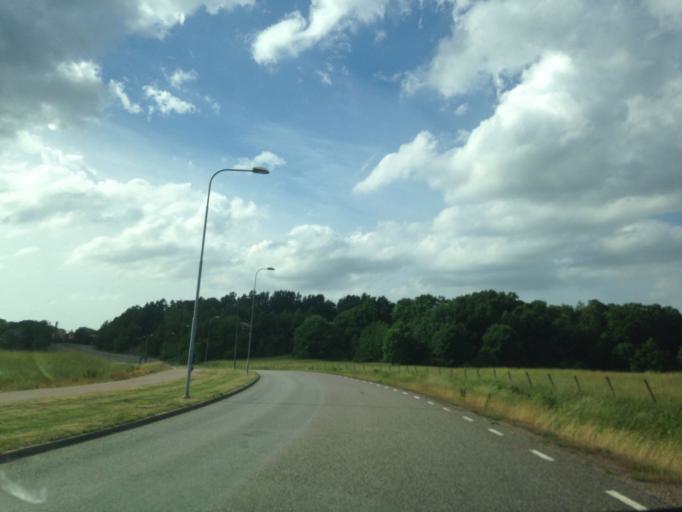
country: SE
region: Vaestra Goetaland
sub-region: Goteborg
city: Goeteborg
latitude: 57.7611
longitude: 11.9370
